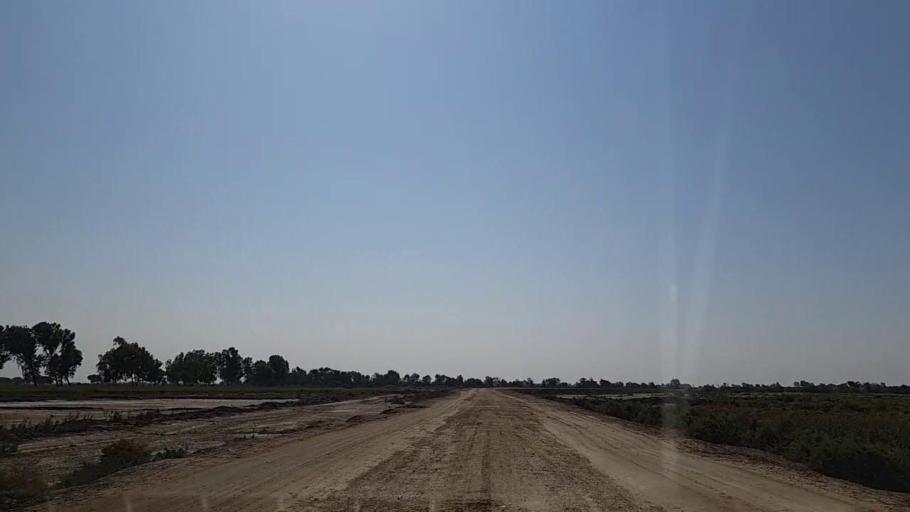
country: PK
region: Sindh
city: Chuhar Jamali
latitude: 24.5005
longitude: 68.0986
